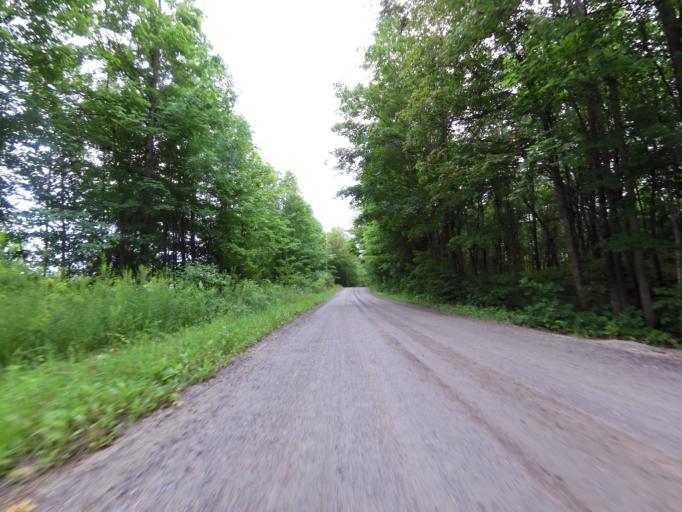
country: CA
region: Ontario
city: Perth
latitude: 45.0482
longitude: -76.3955
